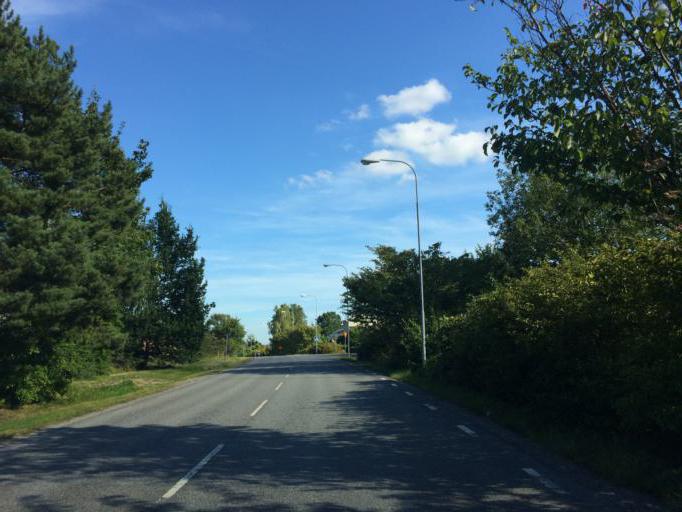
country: SE
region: Stockholm
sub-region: Upplands Vasby Kommun
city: Upplands Vaesby
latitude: 59.4951
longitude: 17.9384
